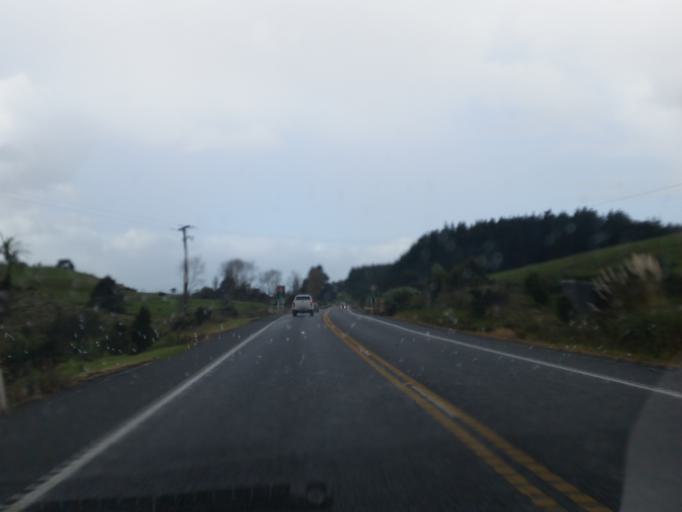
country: NZ
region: Waikato
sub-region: Hauraki District
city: Ngatea
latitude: -37.2788
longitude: 175.3278
